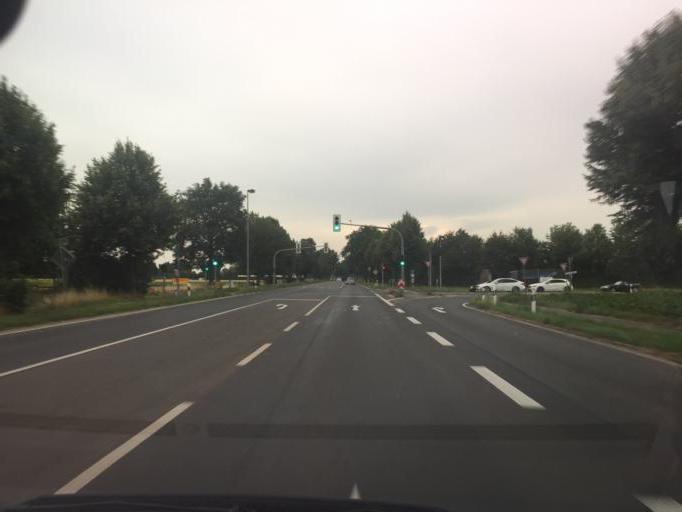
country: DE
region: North Rhine-Westphalia
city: Erkelenz
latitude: 51.1274
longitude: 6.3366
